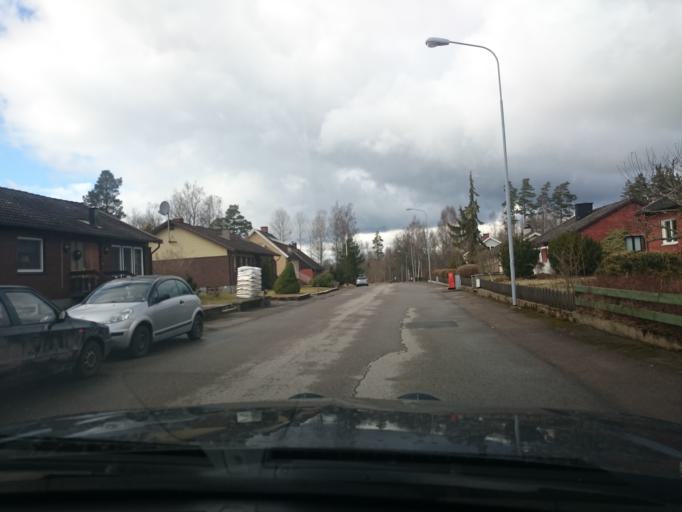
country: SE
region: Joenkoeping
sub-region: Vetlanda Kommun
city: Vetlanda
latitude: 57.3084
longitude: 15.1260
